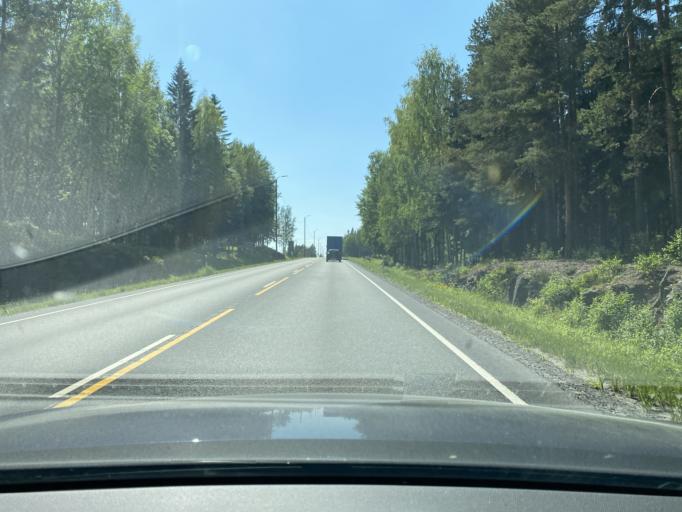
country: FI
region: Pirkanmaa
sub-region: Lounais-Pirkanmaa
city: Mouhijaervi
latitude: 61.3571
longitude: 23.0854
